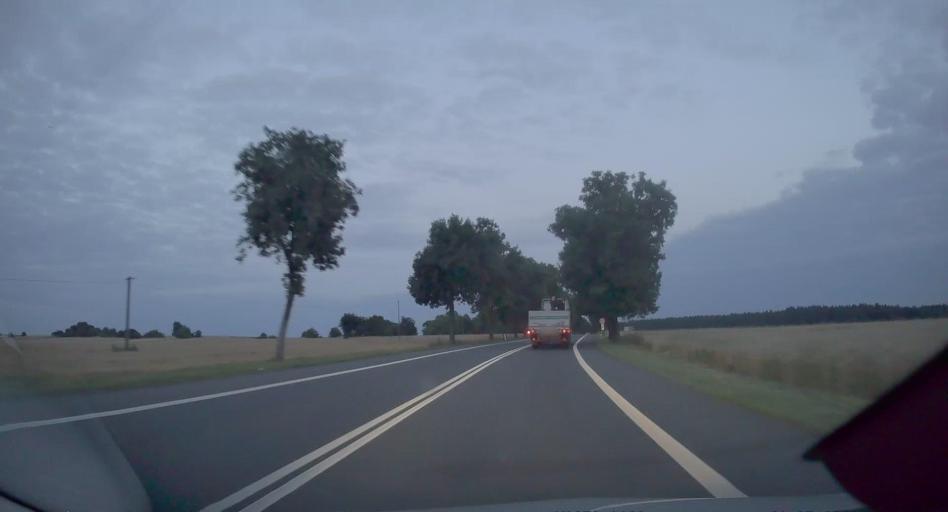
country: PL
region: Silesian Voivodeship
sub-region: Powiat klobucki
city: Opatow
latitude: 50.9497
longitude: 18.8257
